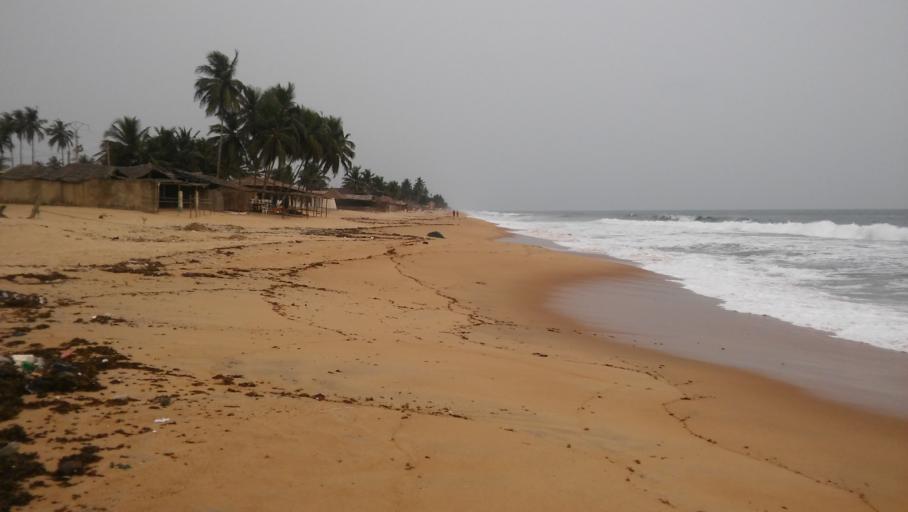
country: CI
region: Sud-Comoe
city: Grand-Bassam
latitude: 5.1977
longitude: -3.7563
